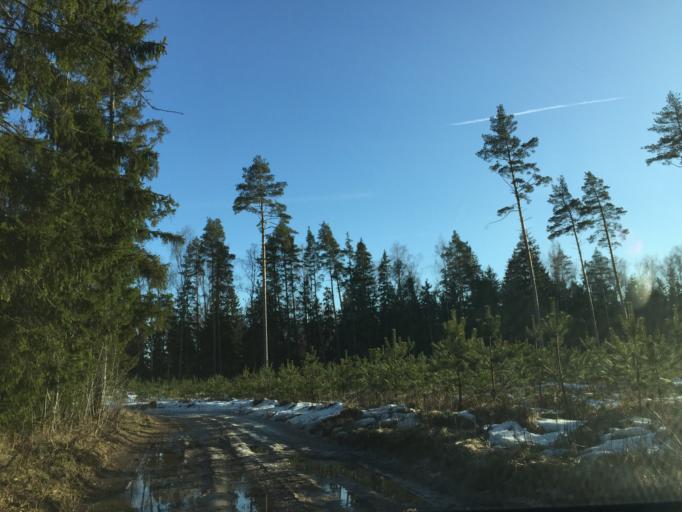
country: LV
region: Lecava
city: Iecava
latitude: 56.6910
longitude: 24.0769
